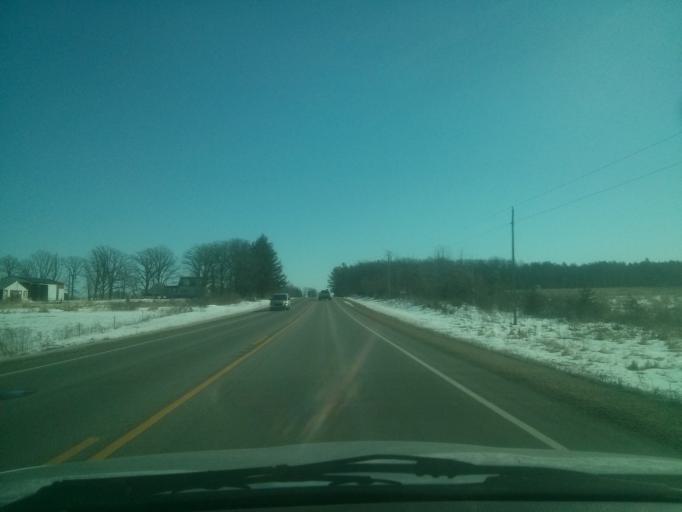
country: US
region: Wisconsin
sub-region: Polk County
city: Clear Lake
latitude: 45.1364
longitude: -92.2912
